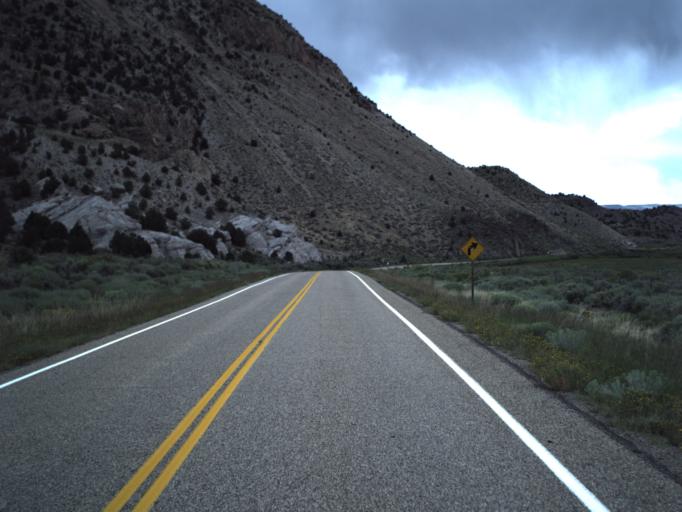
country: US
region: Utah
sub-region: Piute County
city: Junction
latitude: 38.1887
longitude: -112.0950
